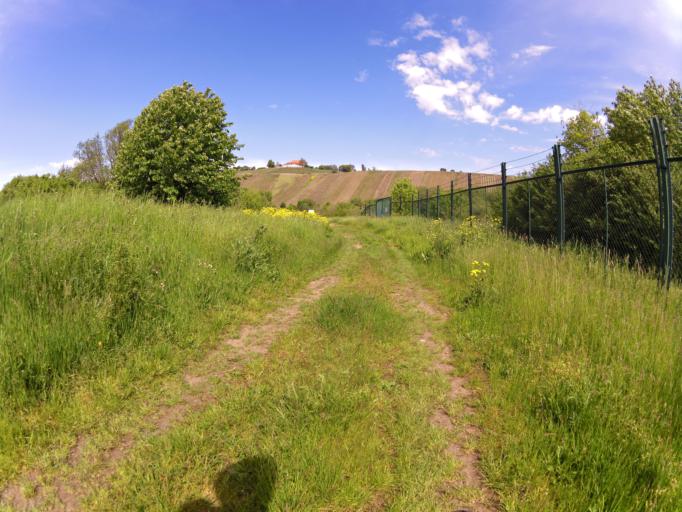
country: DE
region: Bavaria
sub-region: Regierungsbezirk Unterfranken
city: Nordheim
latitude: 49.8622
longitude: 10.1884
